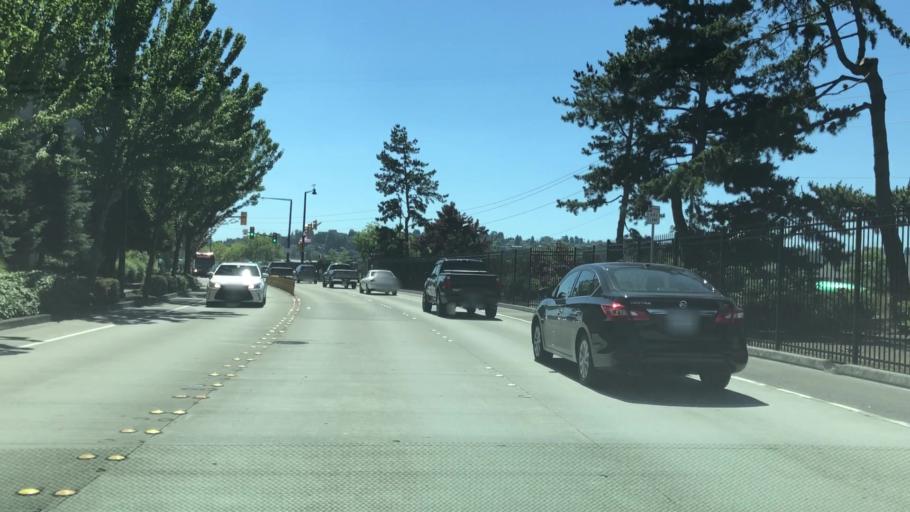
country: US
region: Washington
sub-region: King County
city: Renton
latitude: 47.4988
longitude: -122.2052
